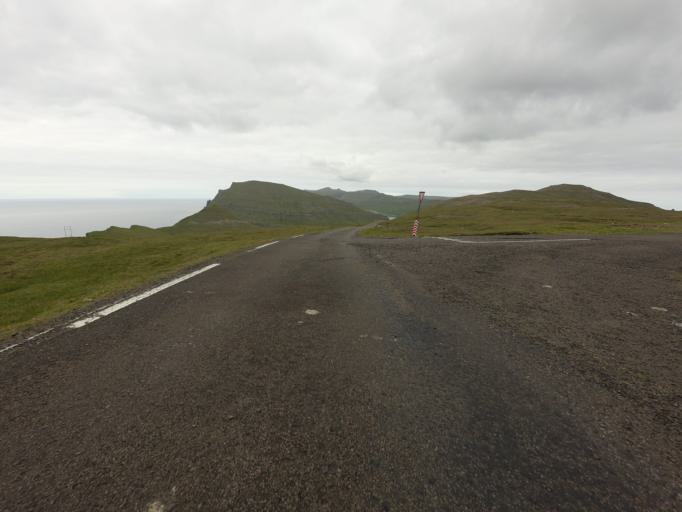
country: FO
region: Suduroy
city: Vagur
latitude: 61.4307
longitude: -6.7590
